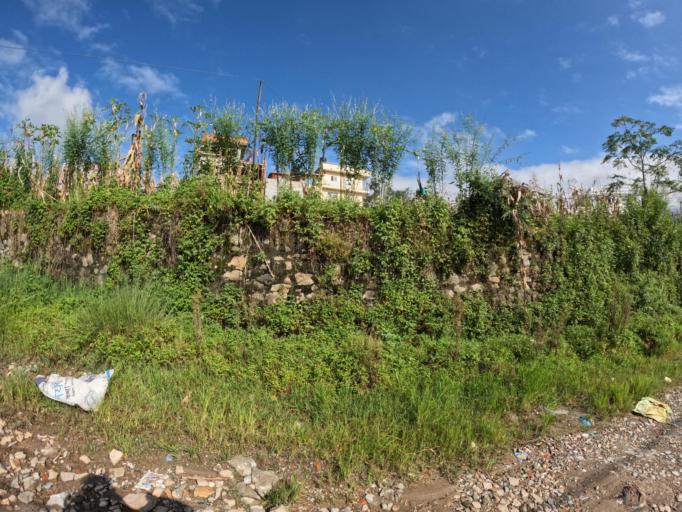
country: NP
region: Central Region
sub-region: Bagmati Zone
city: Kathmandu
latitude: 27.7641
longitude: 85.3341
